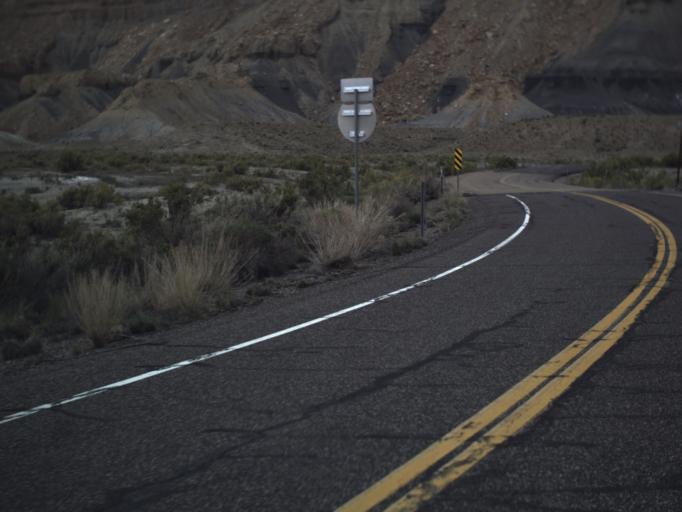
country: US
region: Utah
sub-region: Emery County
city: Ferron
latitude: 38.8138
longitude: -111.2108
